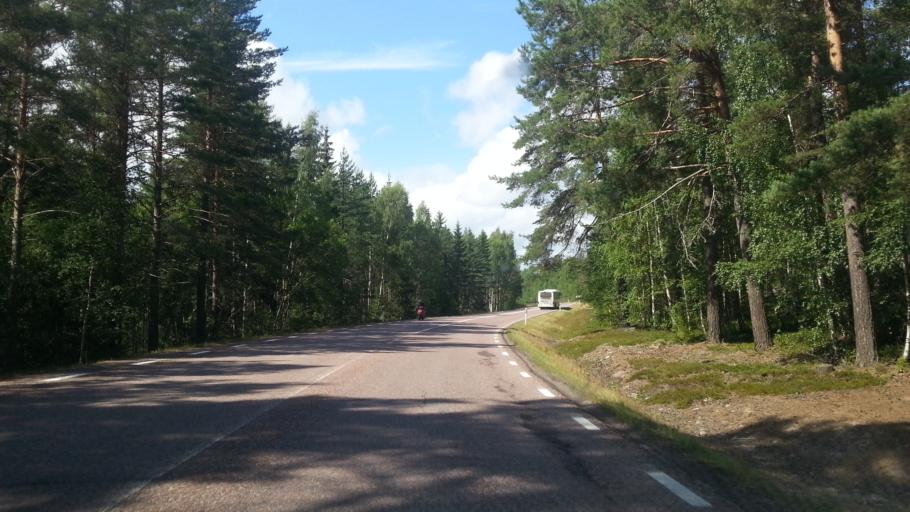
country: SE
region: Dalarna
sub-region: Faluns Kommun
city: Falun
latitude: 60.6125
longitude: 15.7327
